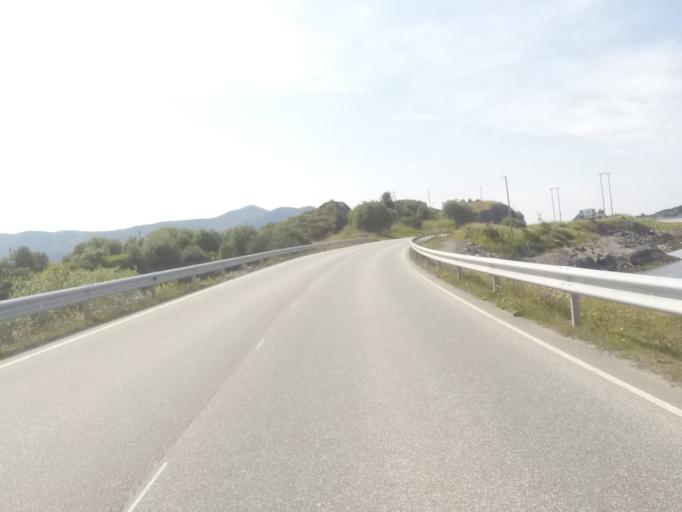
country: NO
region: More og Romsdal
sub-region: Eide
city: Eide
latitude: 63.0108
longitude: 7.3170
